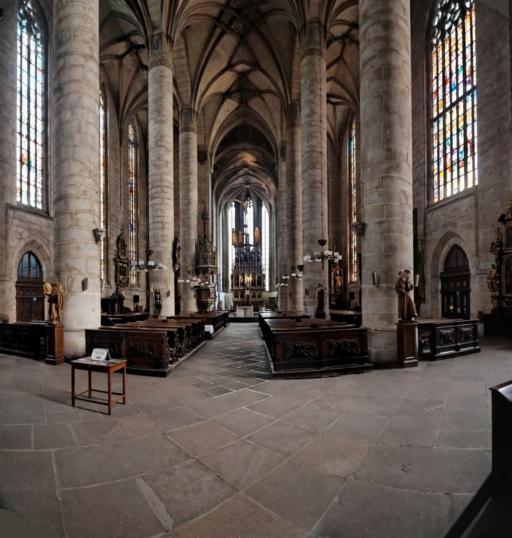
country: CZ
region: Plzensky
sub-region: Okres Plzen-Mesto
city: Pilsen
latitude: 49.7475
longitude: 13.3773
